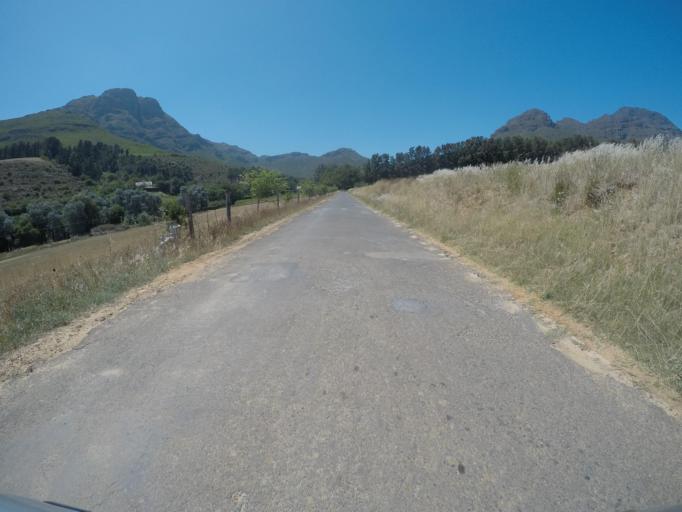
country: ZA
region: Western Cape
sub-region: Cape Winelands District Municipality
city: Stellenbosch
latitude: -34.0018
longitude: 18.8859
